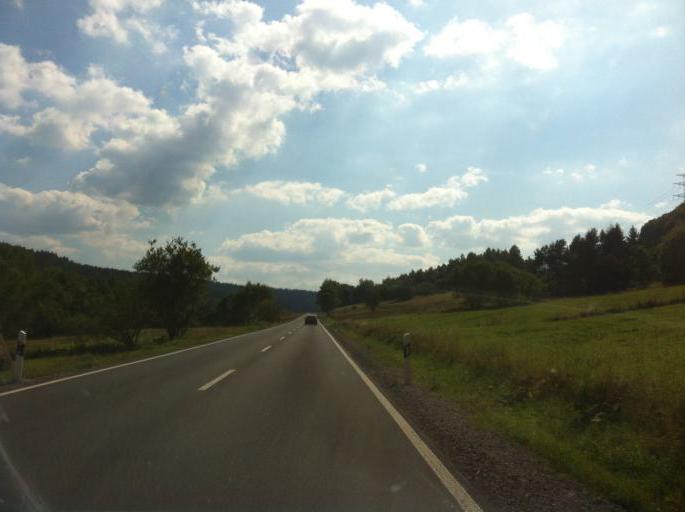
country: DE
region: Thuringia
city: Mohrenbach
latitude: 50.6160
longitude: 10.9938
